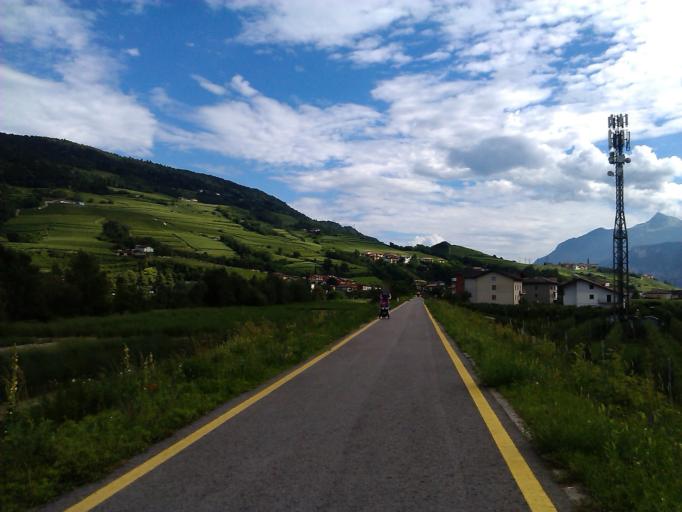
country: IT
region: Trentino-Alto Adige
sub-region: Provincia di Trento
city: Nave San Rocco
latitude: 46.1721
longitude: 11.1108
